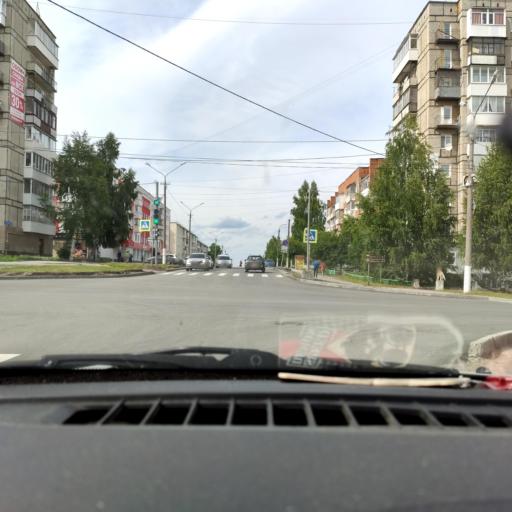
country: RU
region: Perm
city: Chusovoy
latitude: 58.2719
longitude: 57.8082
